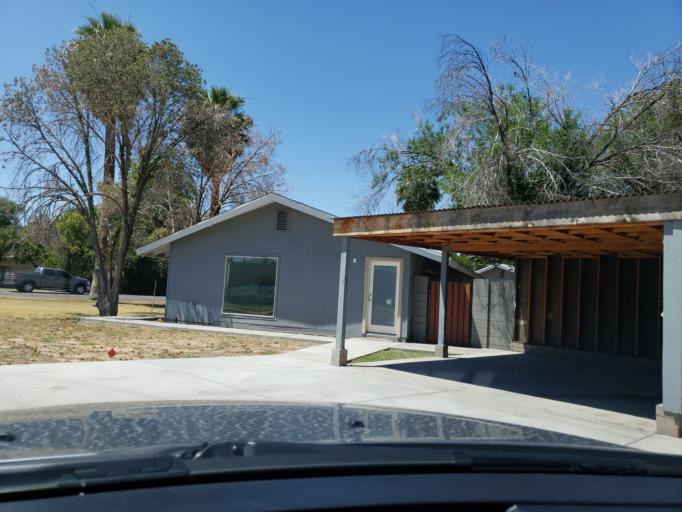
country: US
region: Arizona
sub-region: Maricopa County
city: Phoenix
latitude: 33.5244
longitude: -112.0869
